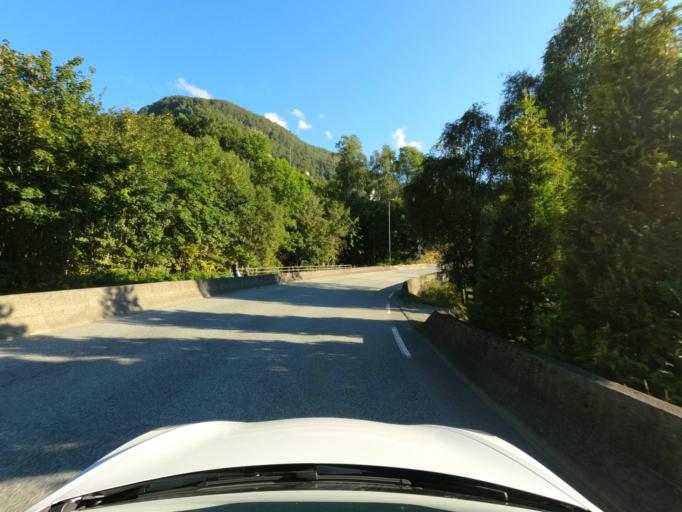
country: NO
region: Hordaland
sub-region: Ullensvang
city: Kinsarvik
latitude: 60.3210
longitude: 6.6557
